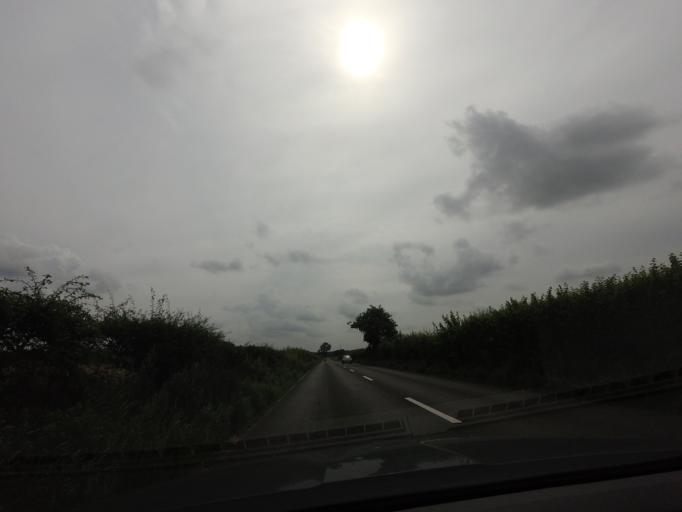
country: GB
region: England
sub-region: Shropshire
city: Tong
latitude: 52.6920
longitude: -2.3168
